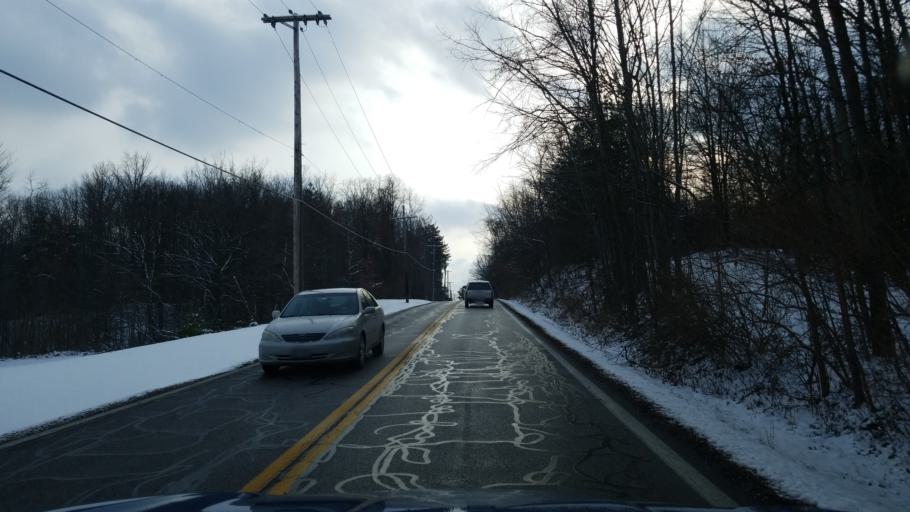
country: US
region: Ohio
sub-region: Cuyahoga County
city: Strongsville
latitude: 41.3403
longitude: -81.8443
